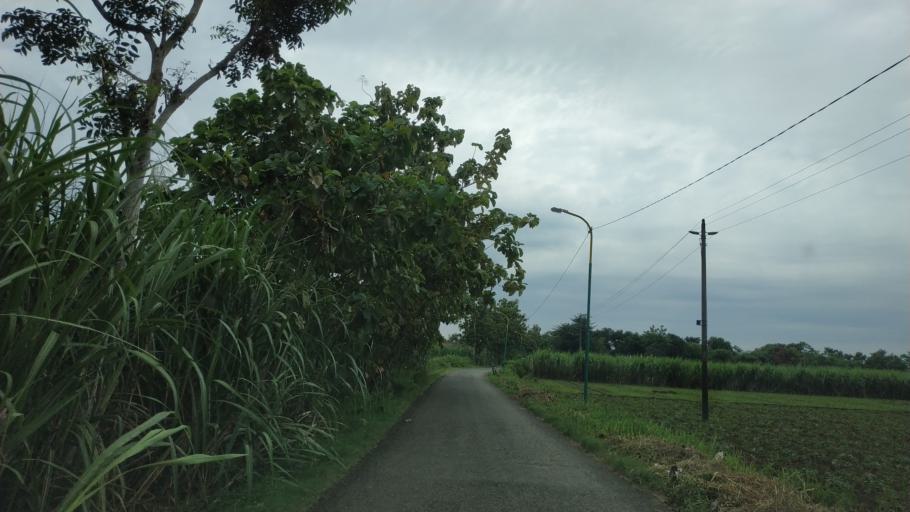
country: ID
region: Central Java
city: Krajan Tegalombo
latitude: -6.4257
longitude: 110.9843
